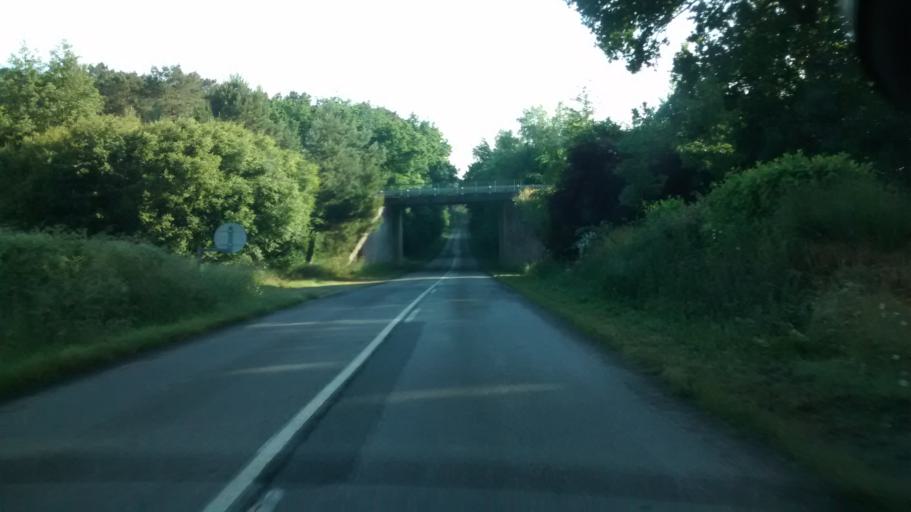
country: FR
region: Brittany
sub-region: Departement du Morbihan
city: Molac
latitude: 47.7693
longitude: -2.4339
